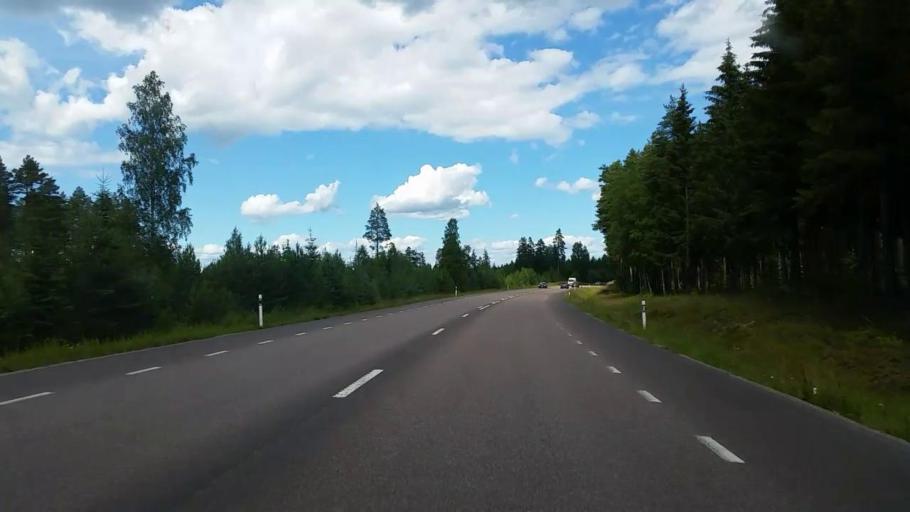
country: SE
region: Dalarna
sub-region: Gagnefs Kommun
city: Gagnef
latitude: 60.6431
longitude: 15.0584
